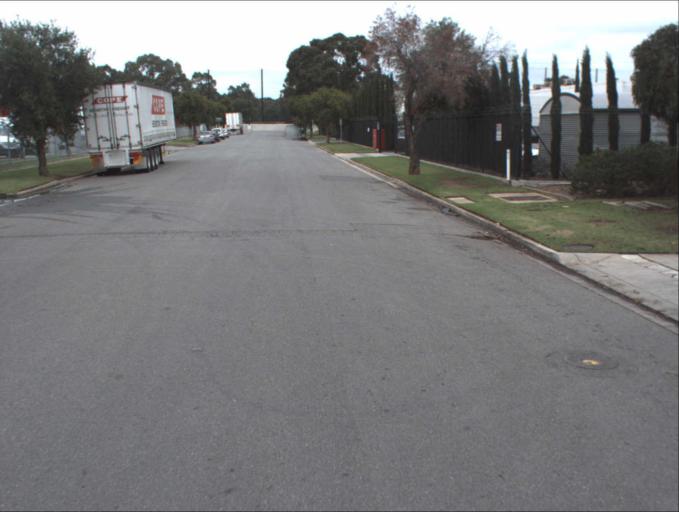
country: AU
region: South Australia
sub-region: Port Adelaide Enfield
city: Blair Athol
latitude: -34.8629
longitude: 138.5719
